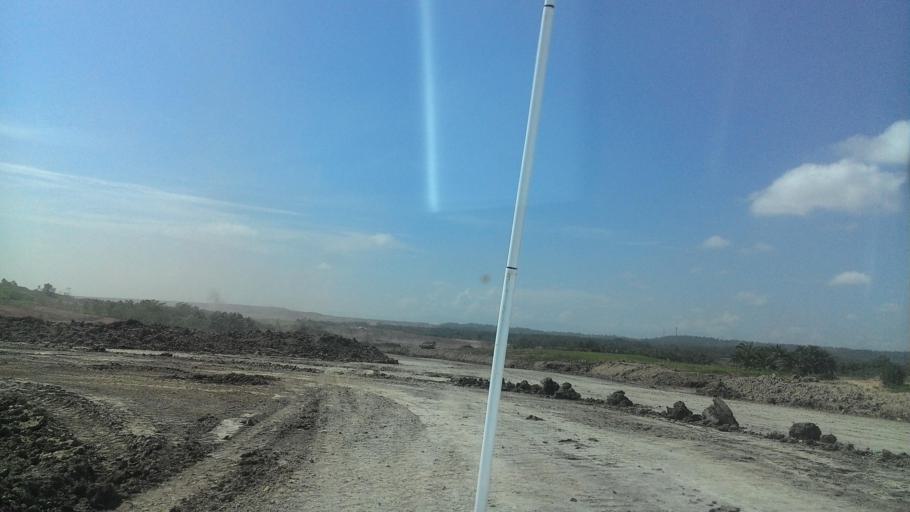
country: ID
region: South Kalimantan
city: Tanta
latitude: -2.1832
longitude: 115.4690
